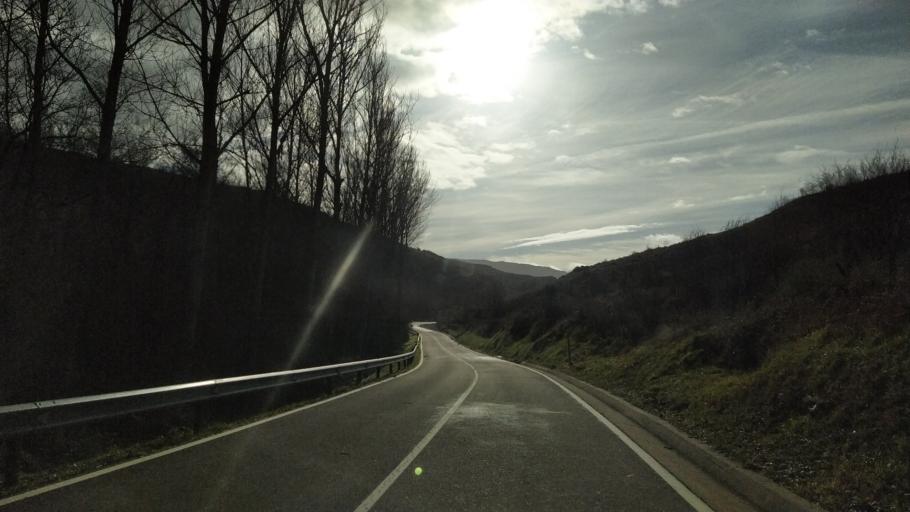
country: ES
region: Cantabria
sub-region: Provincia de Cantabria
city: San Martin de Elines
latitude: 42.8527
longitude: -3.9113
